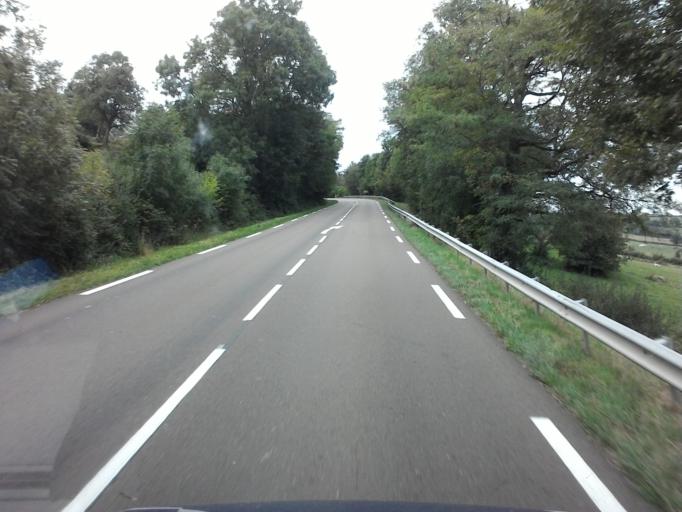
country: FR
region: Bourgogne
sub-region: Departement de Saone-et-Loire
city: Saint-Eusebe
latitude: 46.6296
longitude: 4.4648
